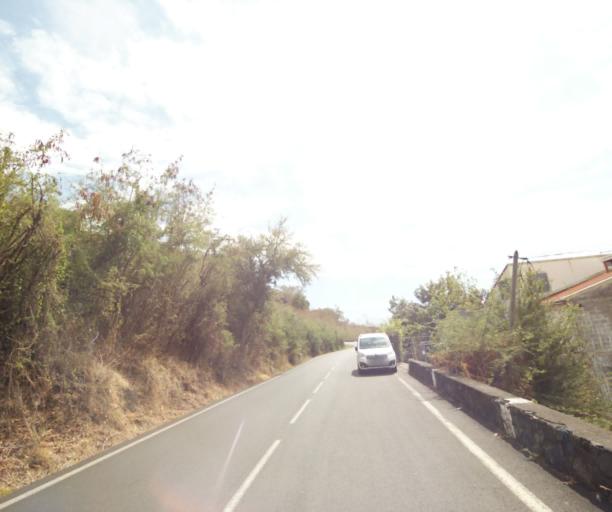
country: RE
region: Reunion
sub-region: Reunion
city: Saint-Paul
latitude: -21.0162
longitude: 55.2783
